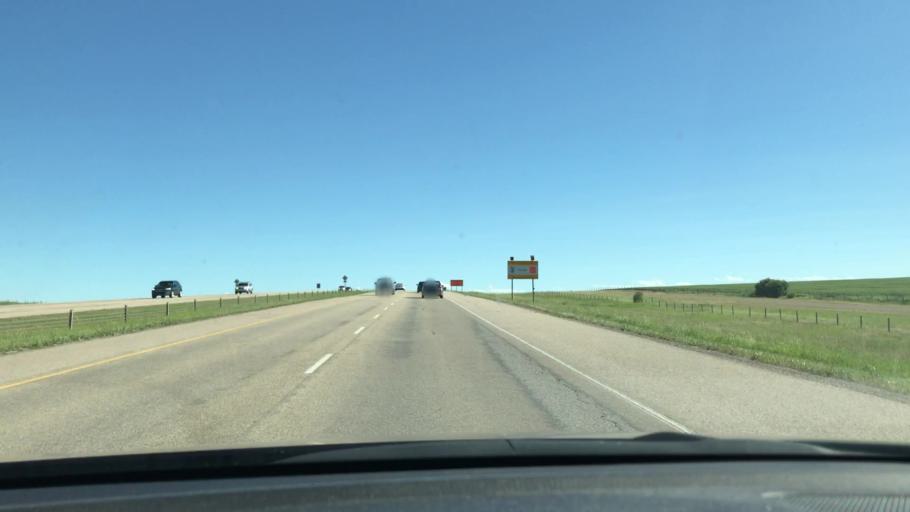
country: CA
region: Alberta
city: Carstairs
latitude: 51.5764
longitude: -114.0253
